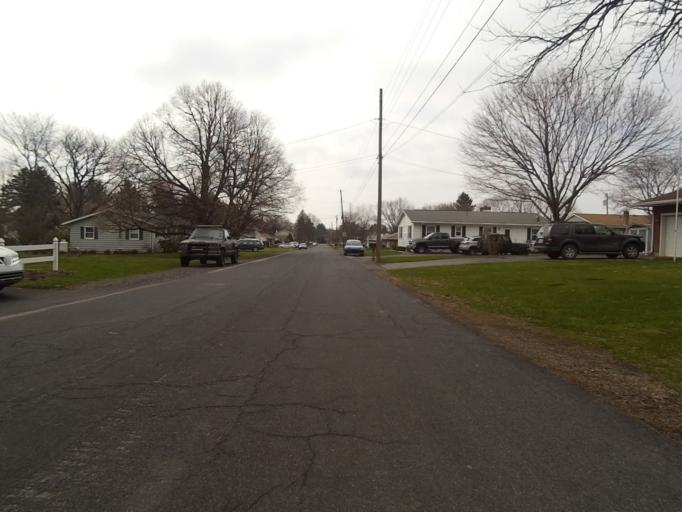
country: US
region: Pennsylvania
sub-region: Centre County
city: Boalsburg
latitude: 40.7874
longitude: -77.7912
